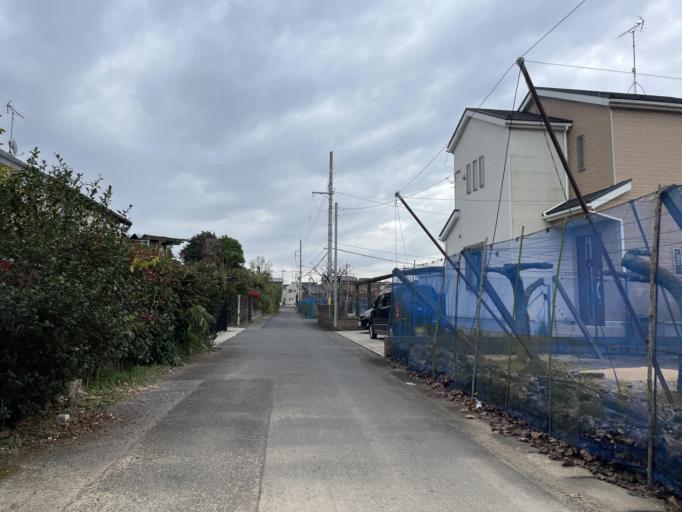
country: JP
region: Saitama
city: Shiraoka
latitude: 36.0301
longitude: 139.6544
